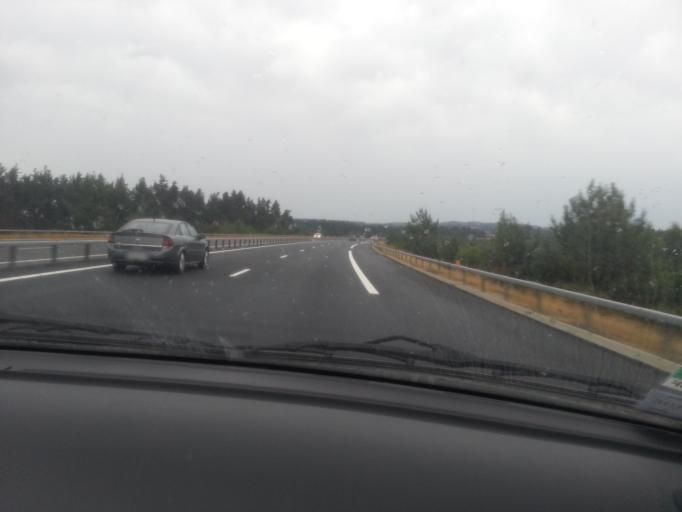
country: FR
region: Languedoc-Roussillon
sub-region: Departement de la Lozere
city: Aumont-Aubrac
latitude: 44.6789
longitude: 3.2601
